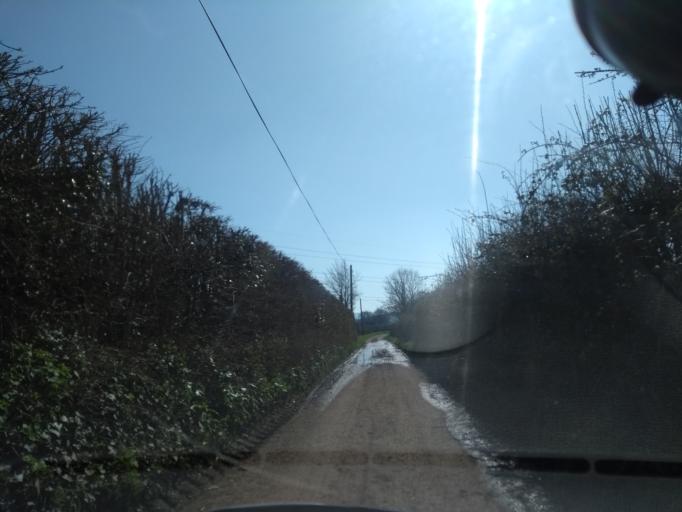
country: GB
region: England
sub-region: Somerset
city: Taunton
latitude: 51.0455
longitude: -3.1182
